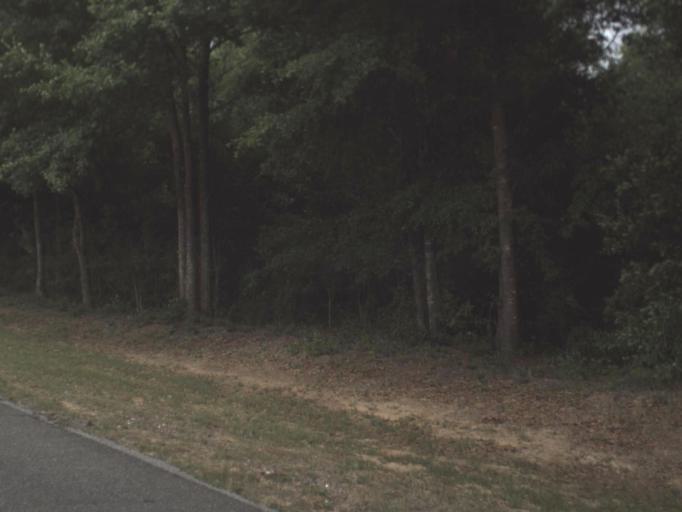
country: US
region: Florida
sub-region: Santa Rosa County
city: Point Baker
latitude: 30.7273
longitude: -87.0828
